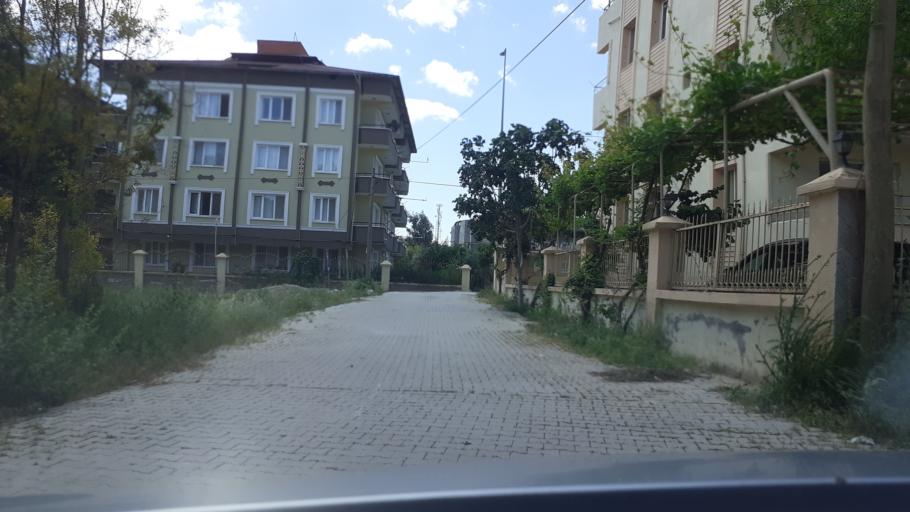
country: TR
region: Hatay
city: Anayazi
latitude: 36.3344
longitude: 36.2037
